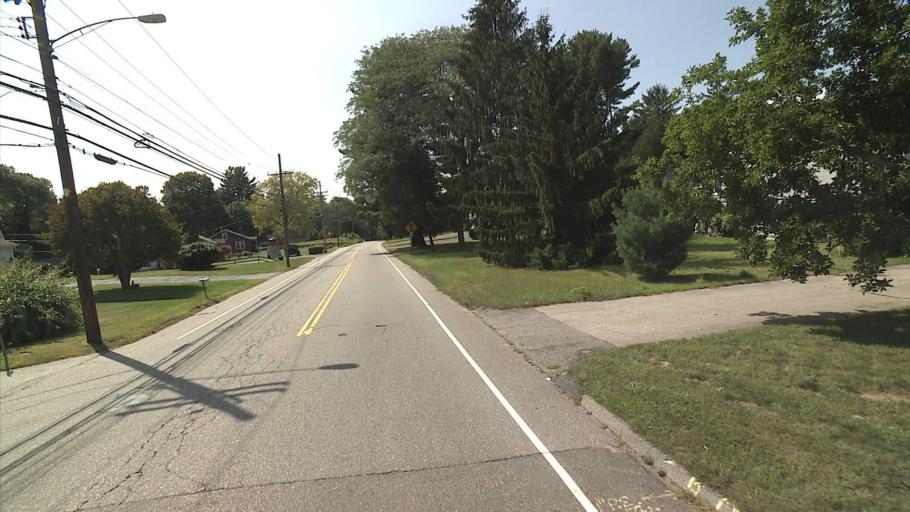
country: US
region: Connecticut
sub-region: New London County
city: Norwich
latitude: 41.5523
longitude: -72.0814
